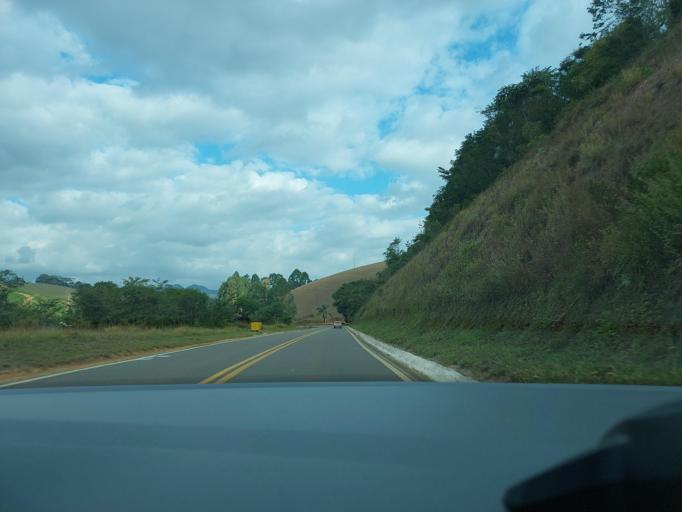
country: BR
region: Minas Gerais
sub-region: Visconde Do Rio Branco
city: Visconde do Rio Branco
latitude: -20.9151
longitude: -42.6403
